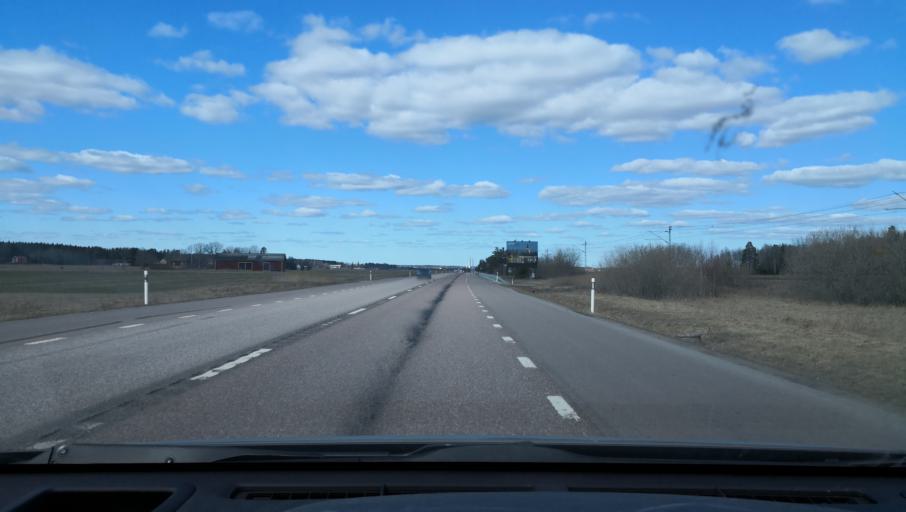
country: SE
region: Vaestmanland
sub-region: Sala Kommun
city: Sala
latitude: 59.8750
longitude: 16.6265
